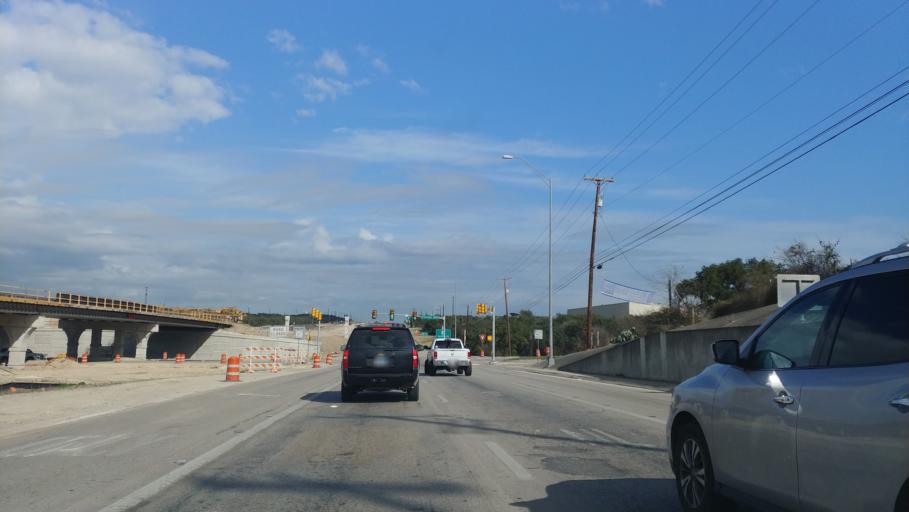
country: US
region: Texas
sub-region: Bexar County
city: Leon Valley
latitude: 29.4645
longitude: -98.7109
